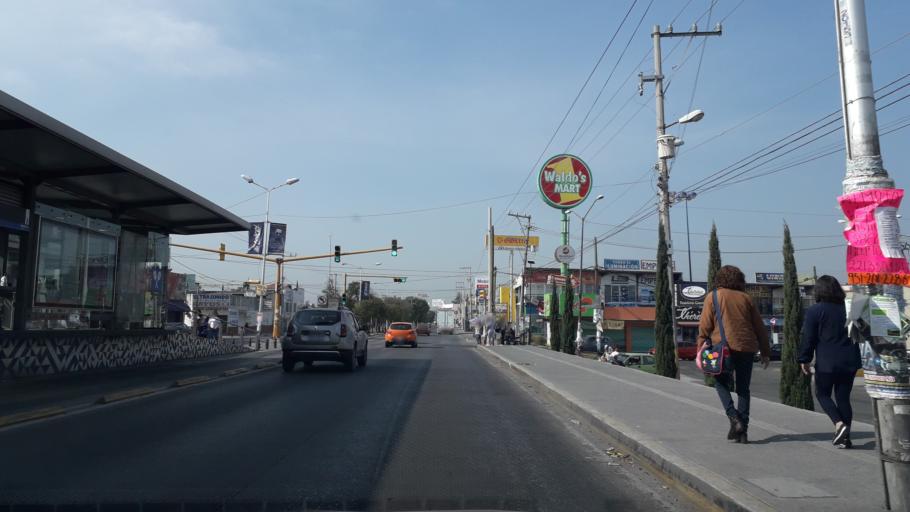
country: MX
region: Puebla
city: Tlazcalancingo
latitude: 19.0037
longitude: -98.2388
